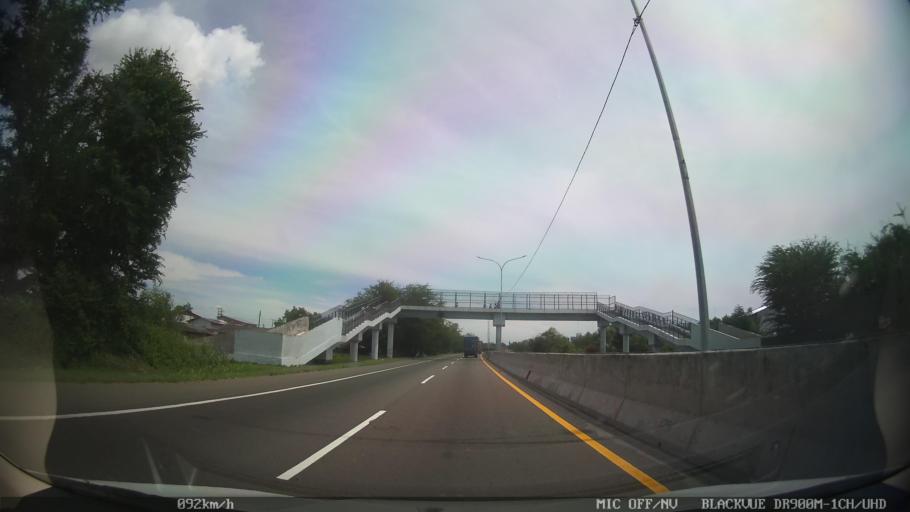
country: ID
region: North Sumatra
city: Belawan
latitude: 3.7623
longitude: 98.6831
